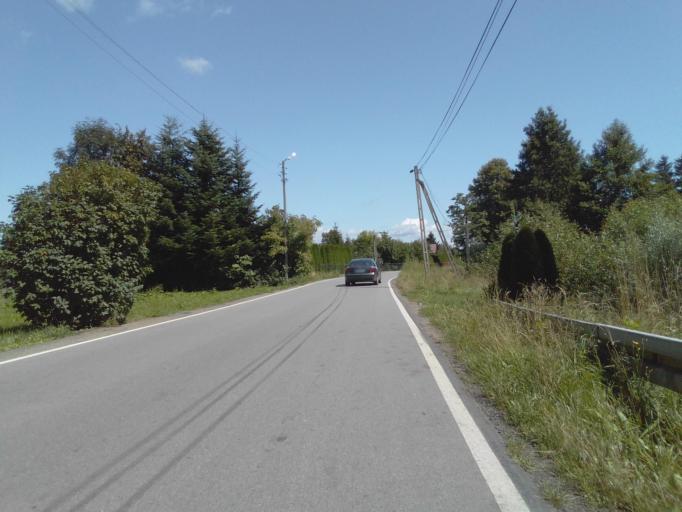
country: PL
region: Subcarpathian Voivodeship
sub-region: Powiat krosnienski
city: Jedlicze
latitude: 49.7003
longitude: 21.6216
